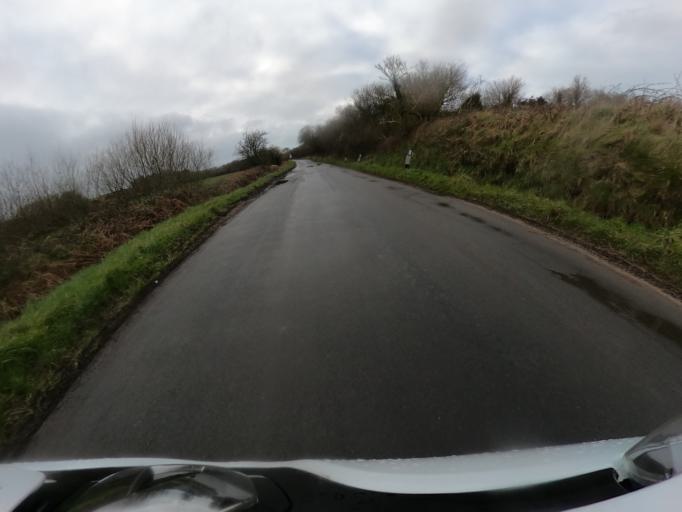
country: IM
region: Ramsey
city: Ramsey
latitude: 54.3641
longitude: -4.4751
